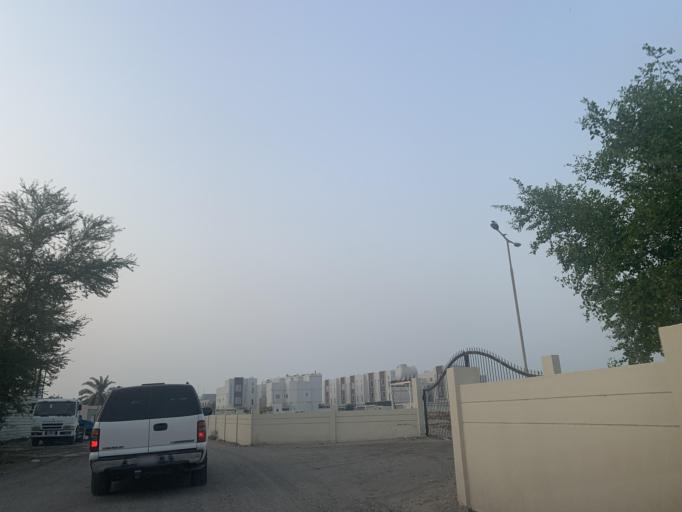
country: BH
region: Manama
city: Jidd Hafs
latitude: 26.2278
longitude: 50.5125
